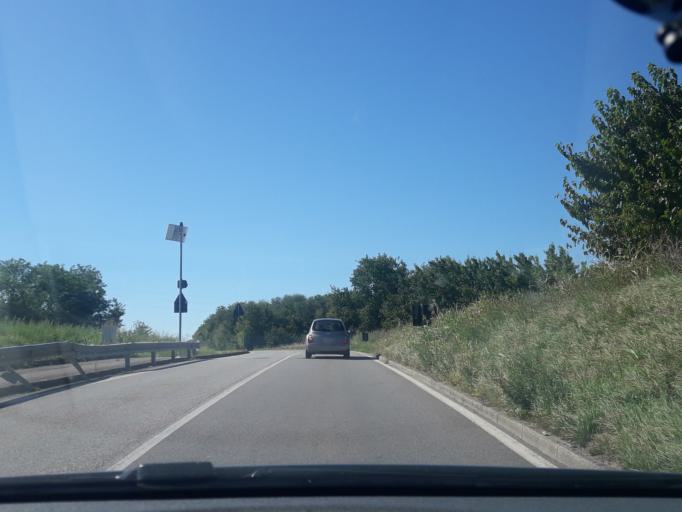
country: IT
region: Friuli Venezia Giulia
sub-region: Provincia di Udine
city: Pradamano
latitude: 46.0325
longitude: 13.2867
